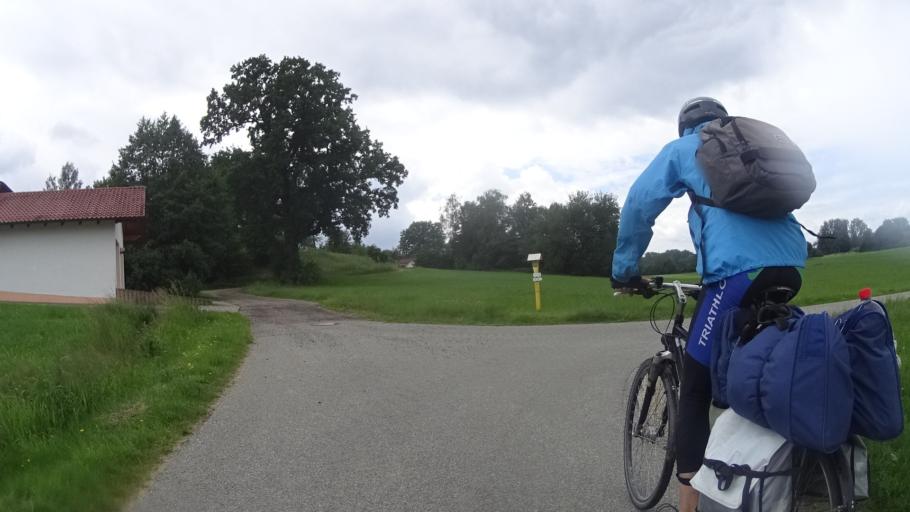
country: DE
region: Bavaria
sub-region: Lower Bavaria
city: Eggenfelden
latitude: 48.4046
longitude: 12.7900
